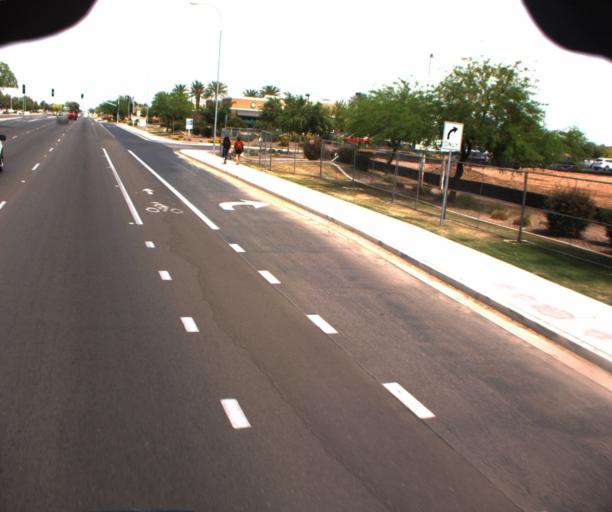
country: US
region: Arizona
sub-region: Maricopa County
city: Sun Lakes
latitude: 33.2498
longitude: -111.8411
